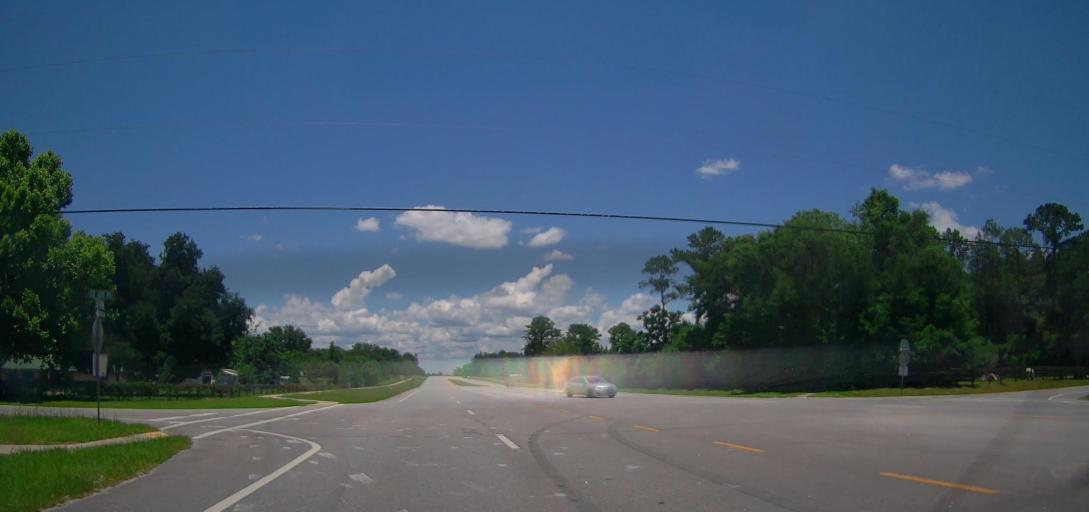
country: US
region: Florida
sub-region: Marion County
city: Belleview
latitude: 29.0385
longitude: -82.0177
